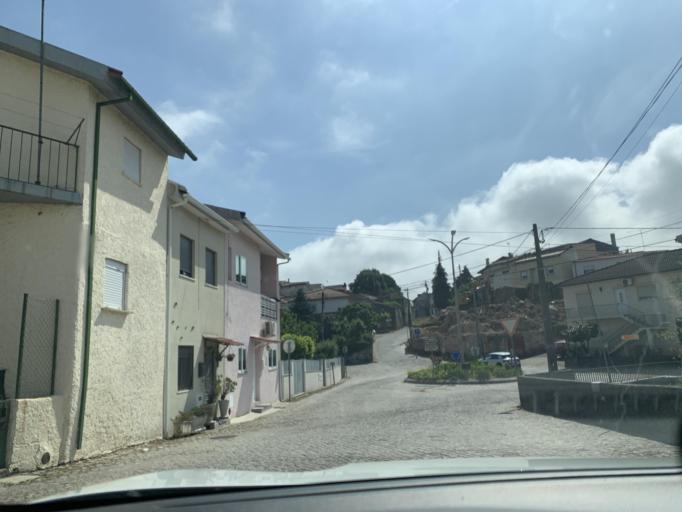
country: PT
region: Viseu
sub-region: Viseu
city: Viseu
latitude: 40.6423
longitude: -7.9015
